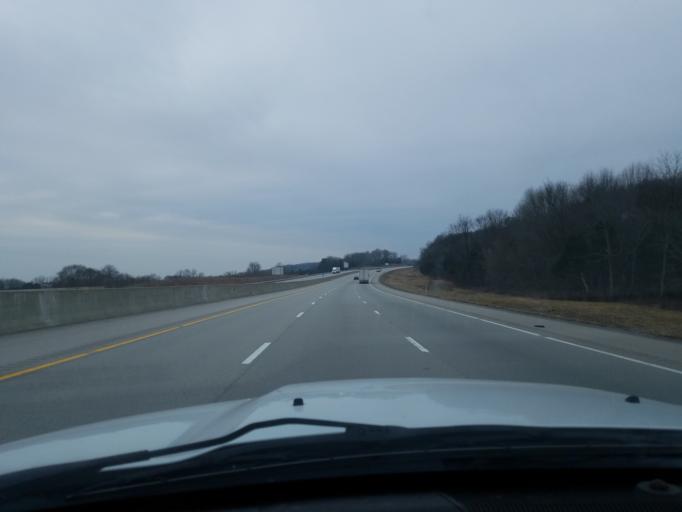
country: US
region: Kentucky
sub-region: Barren County
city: Cave City
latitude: 37.1269
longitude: -85.9885
